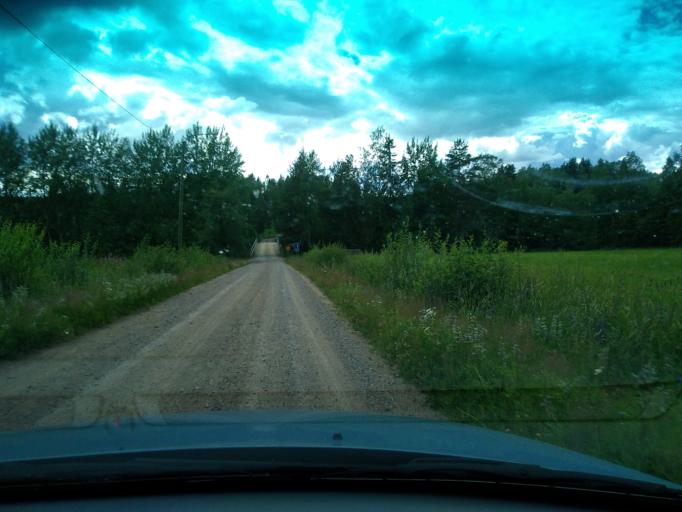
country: FI
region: Central Finland
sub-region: Saarijaervi-Viitasaari
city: Karstula
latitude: 62.7903
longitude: 24.9539
